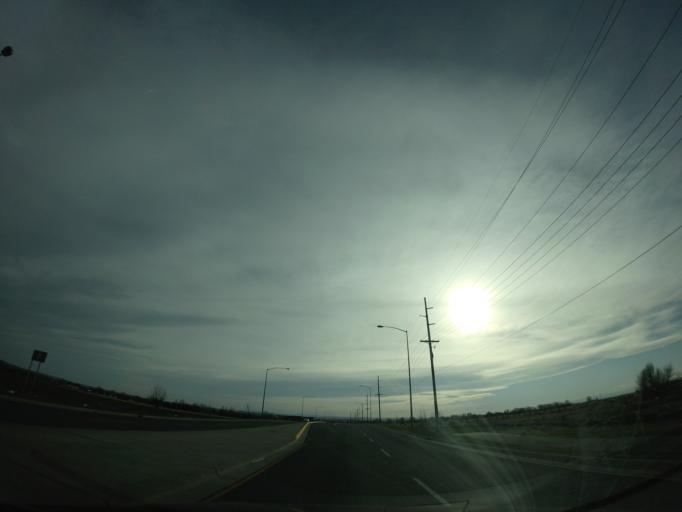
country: US
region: Montana
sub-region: Yellowstone County
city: Billings
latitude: 45.7814
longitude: -108.6177
